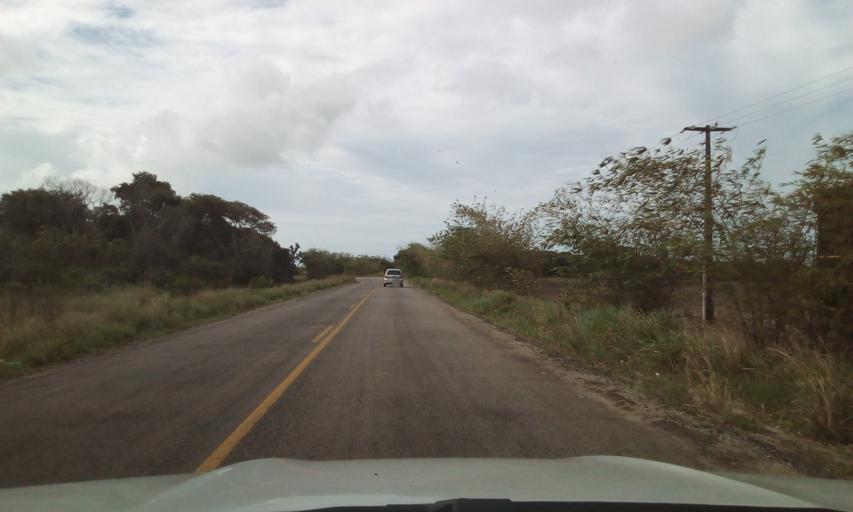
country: BR
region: Paraiba
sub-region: Cabedelo
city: Cabedelo
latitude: -6.9242
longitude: -34.8990
